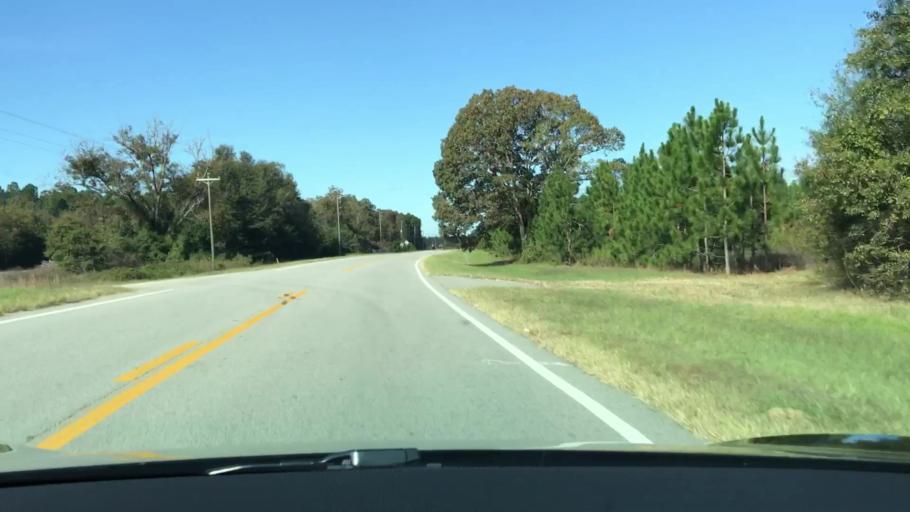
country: US
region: Georgia
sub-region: Glascock County
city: Gibson
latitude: 33.3077
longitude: -82.5317
